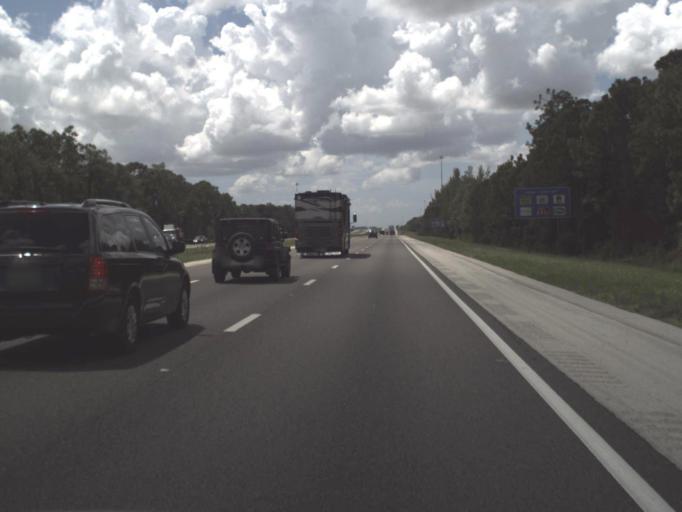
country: US
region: Florida
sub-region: Collier County
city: Vineyards
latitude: 26.2240
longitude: -81.7366
